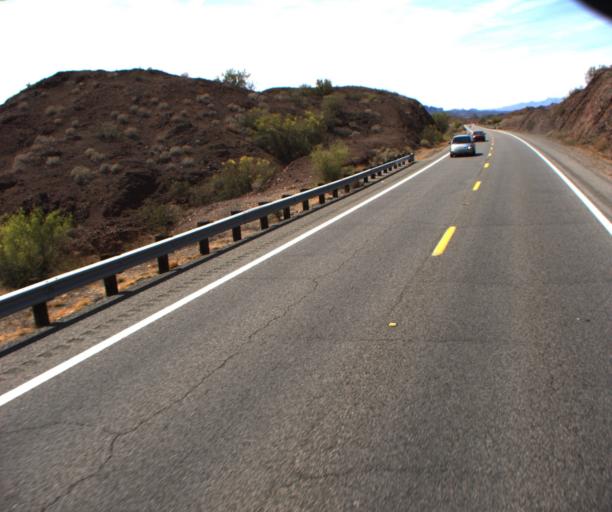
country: US
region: Arizona
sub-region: La Paz County
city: Cienega Springs
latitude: 34.3228
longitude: -114.1217
